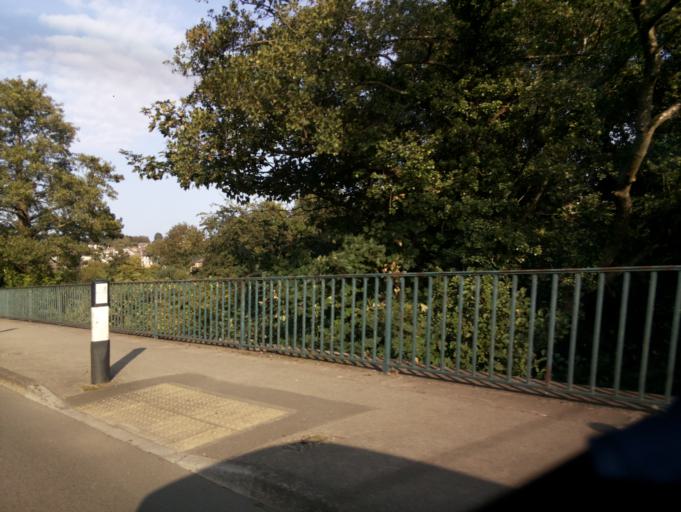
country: GB
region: Wales
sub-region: Torfaen County Borough
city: Cwmbran
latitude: 51.6582
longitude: -3.0136
